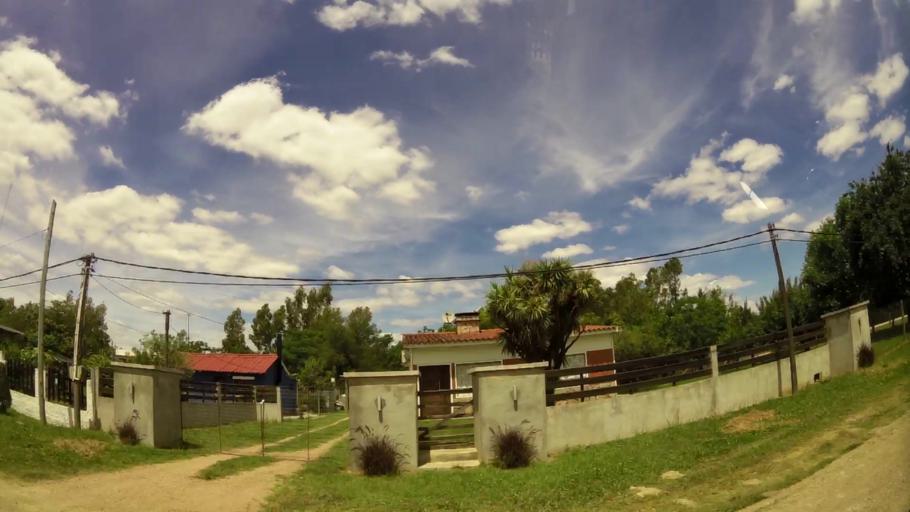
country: UY
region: San Jose
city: Delta del Tigre
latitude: -34.7405
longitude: -56.4415
